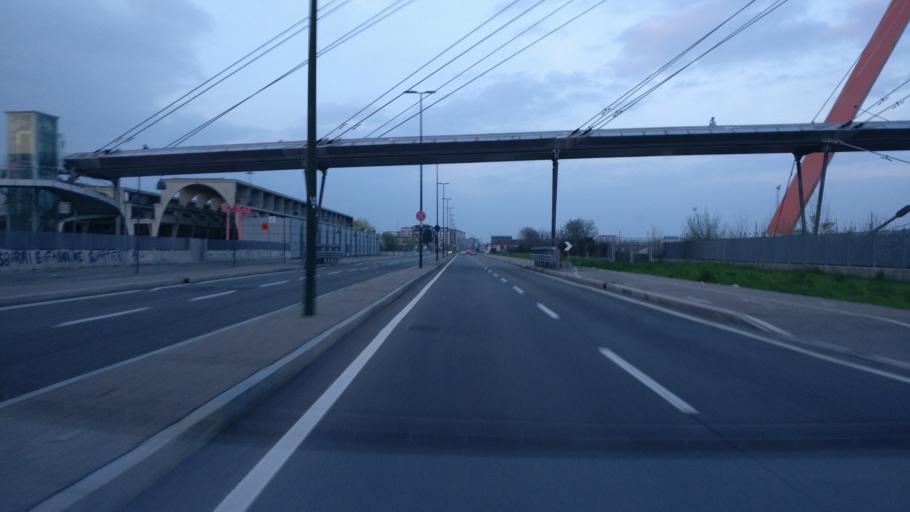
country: IT
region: Piedmont
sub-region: Provincia di Torino
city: Nichelino
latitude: 45.0316
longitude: 7.6578
